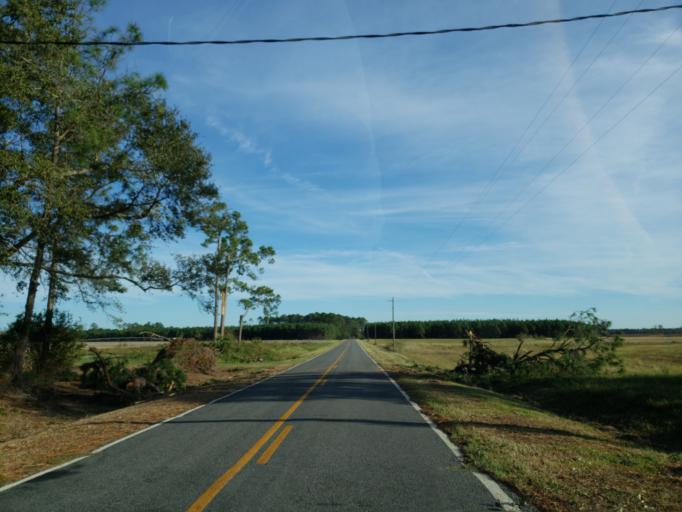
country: US
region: Georgia
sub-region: Dooly County
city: Vienna
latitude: 32.0499
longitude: -83.7597
